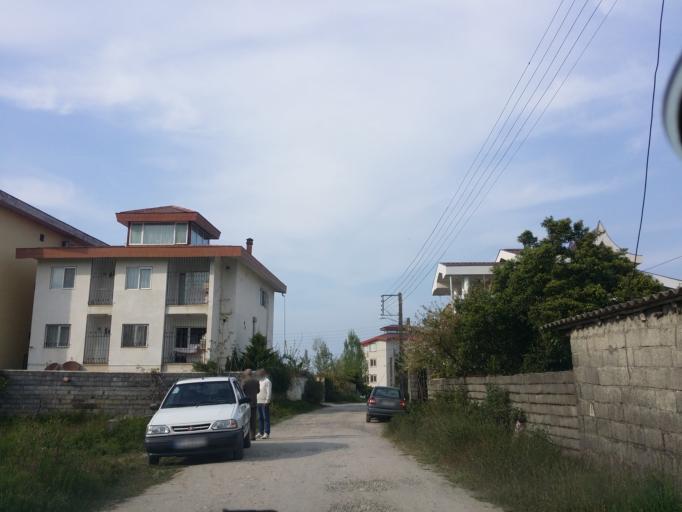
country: IR
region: Mazandaran
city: Chalus
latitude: 36.6832
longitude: 51.3962
